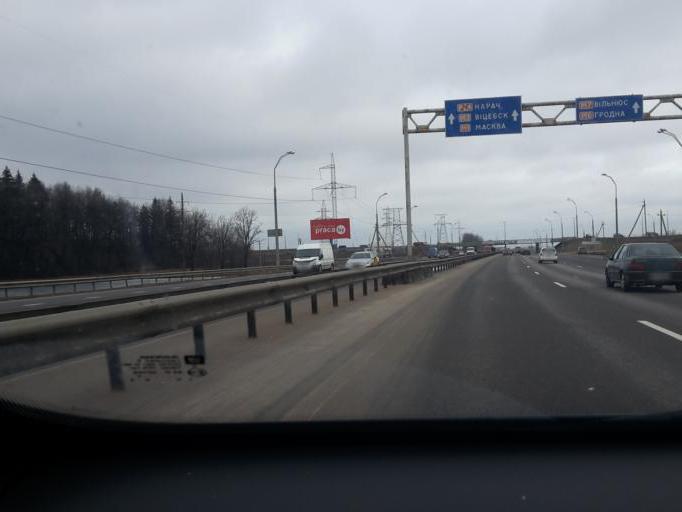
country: BY
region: Minsk
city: Zhdanovichy
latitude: 53.9071
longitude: 27.4077
